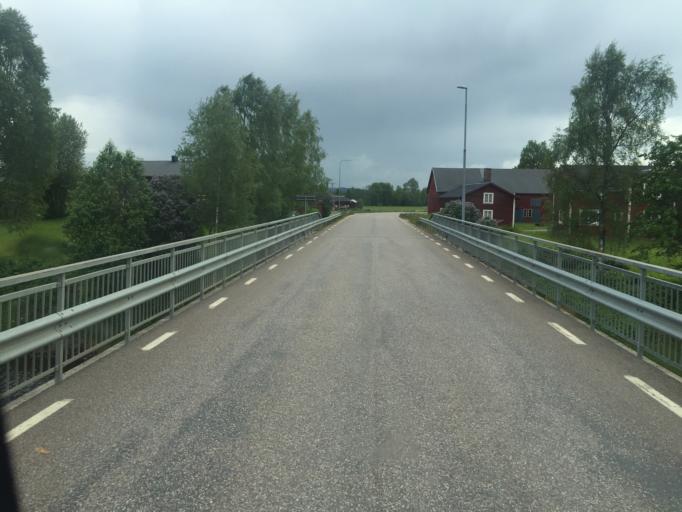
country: SE
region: Dalarna
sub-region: Vansbro Kommun
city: Vansbro
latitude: 60.4696
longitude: 14.0073
